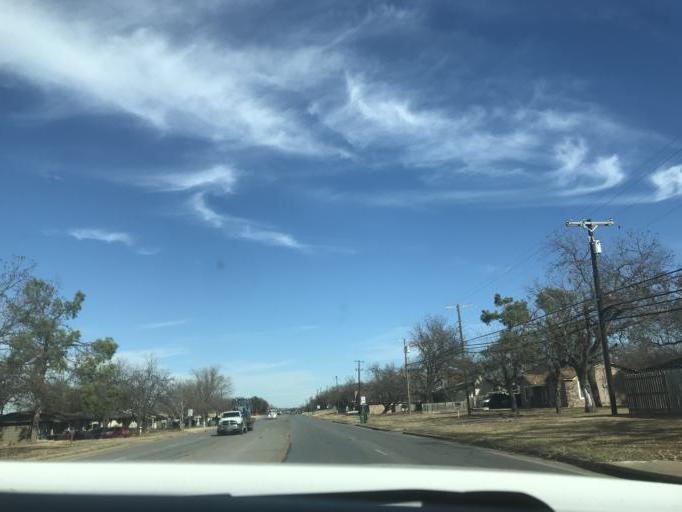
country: US
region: Texas
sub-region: Erath County
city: Stephenville
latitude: 32.2251
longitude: -98.2241
